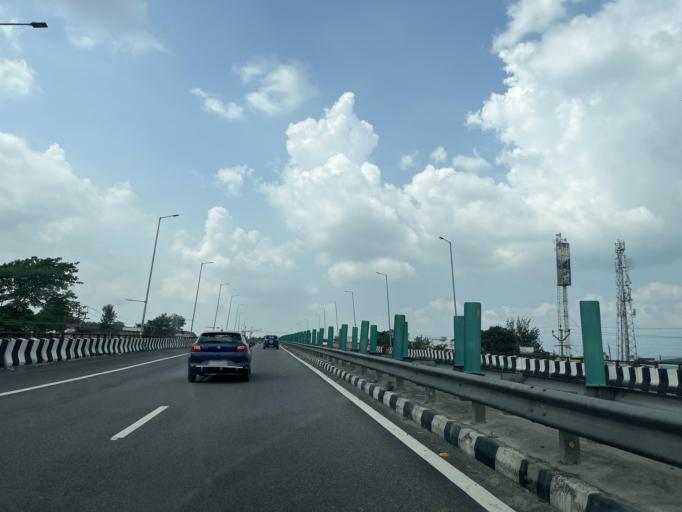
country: IN
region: Uttarakhand
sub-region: Dehradun
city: Raipur
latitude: 30.2619
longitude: 78.0871
